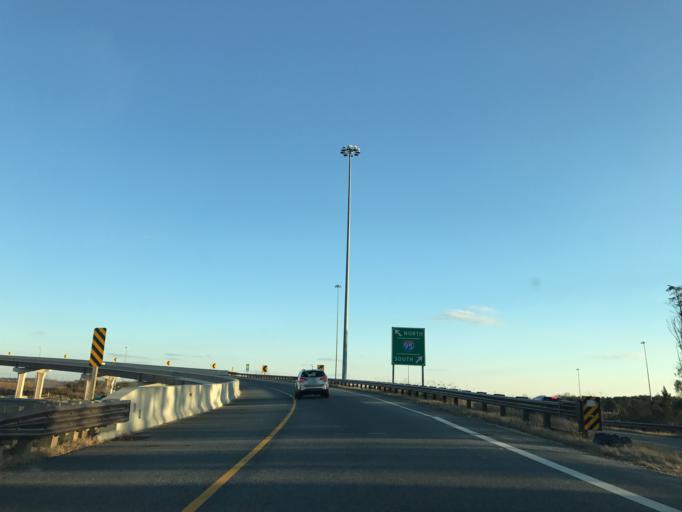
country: US
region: Maryland
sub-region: Prince George's County
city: West Laurel
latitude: 39.0732
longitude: -76.9084
